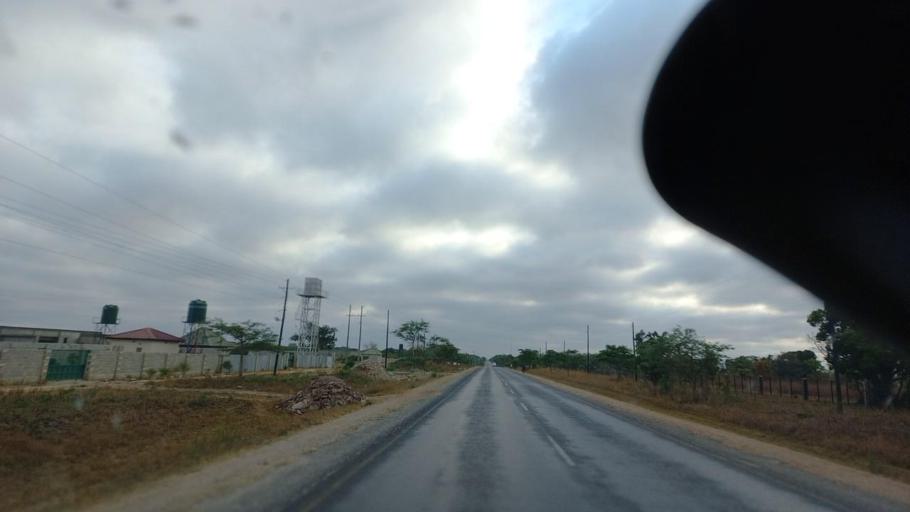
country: ZM
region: Lusaka
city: Chongwe
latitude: -15.3512
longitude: 28.4937
